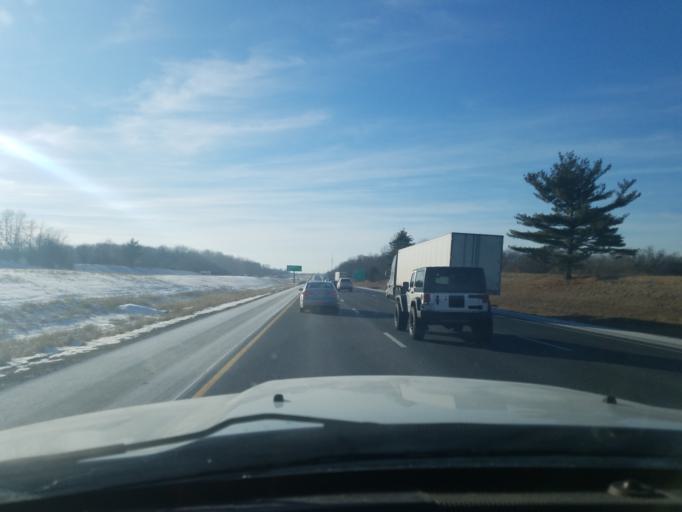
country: US
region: Indiana
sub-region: Hancock County
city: Fortville
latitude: 39.9914
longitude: -85.8948
